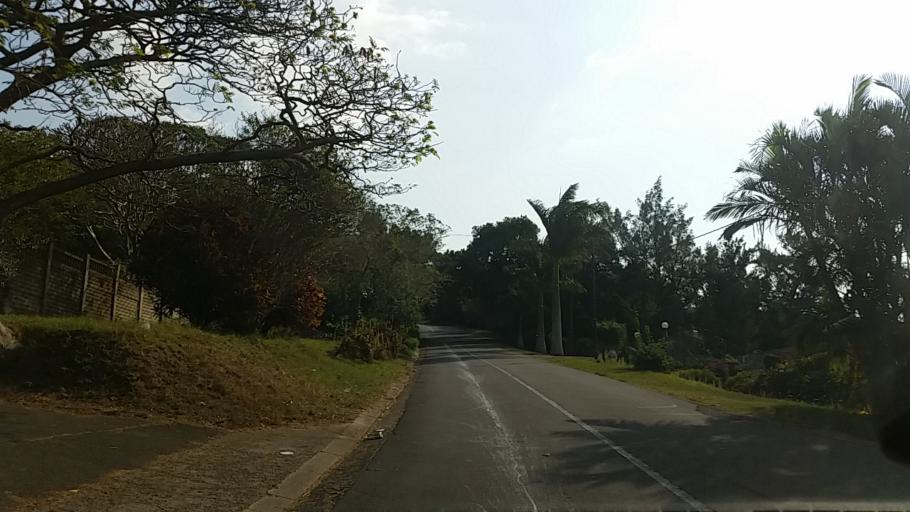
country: ZA
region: KwaZulu-Natal
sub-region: eThekwini Metropolitan Municipality
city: Berea
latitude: -29.8397
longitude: 30.9454
